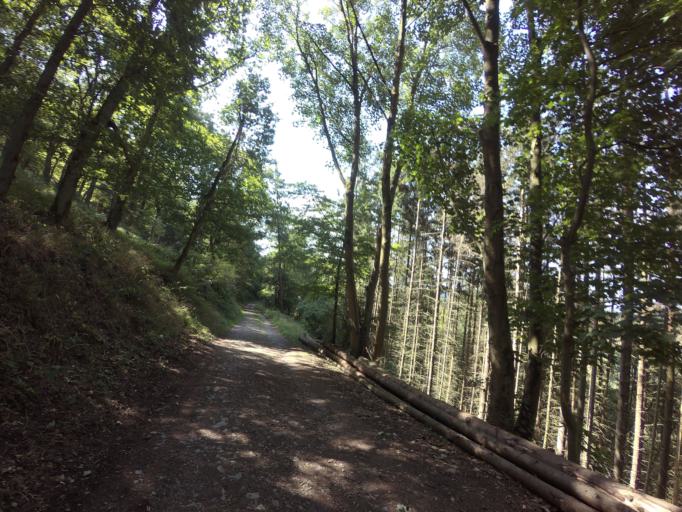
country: DE
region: North Rhine-Westphalia
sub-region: Regierungsbezirk Koln
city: Simmerath
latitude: 50.5932
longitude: 6.3880
